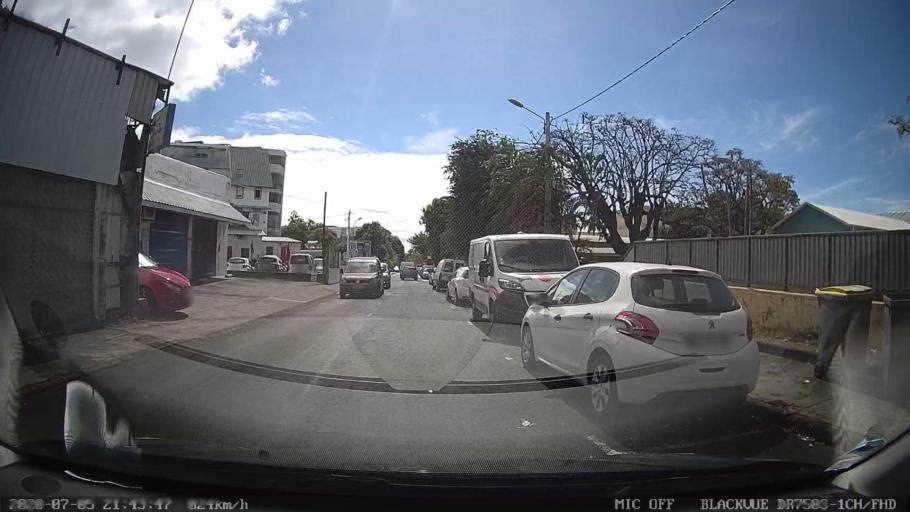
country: RE
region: Reunion
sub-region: Reunion
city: Saint-Denis
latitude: -20.8895
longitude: 55.4799
